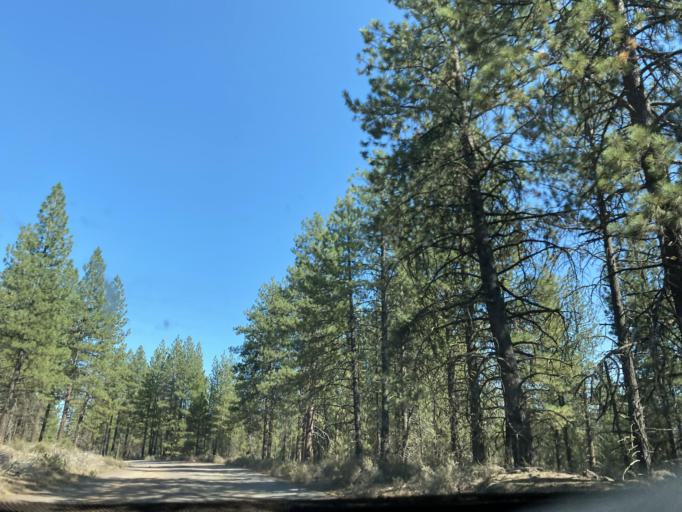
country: US
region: Oregon
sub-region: Deschutes County
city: Sunriver
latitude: 43.8709
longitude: -121.4777
